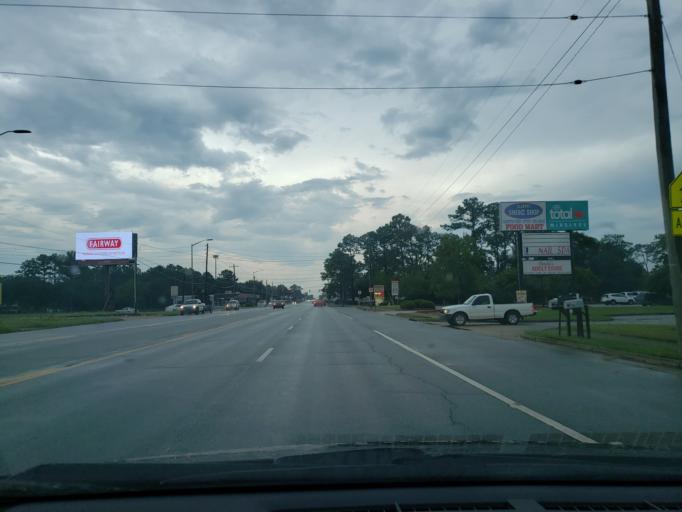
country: US
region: Georgia
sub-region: Dougherty County
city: Albany
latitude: 31.6068
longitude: -84.1759
